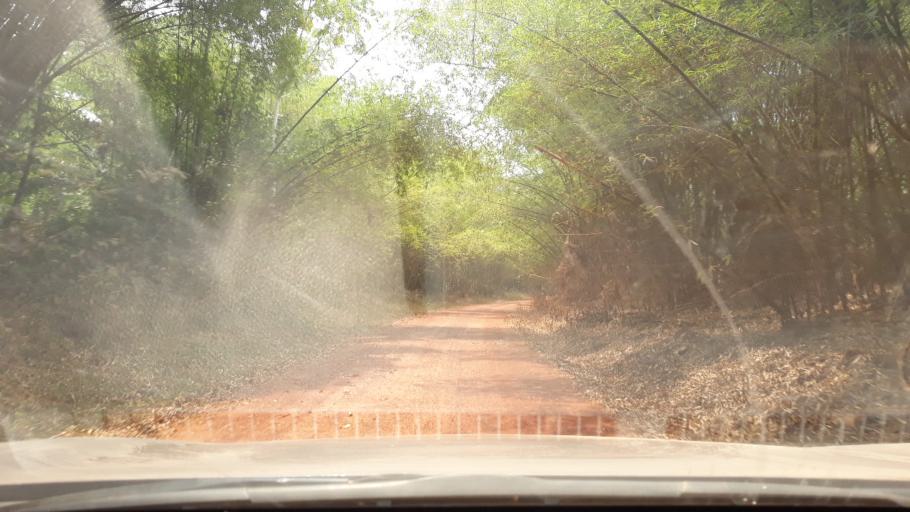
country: CD
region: Eastern Province
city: Buta
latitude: 2.3014
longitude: 25.0306
